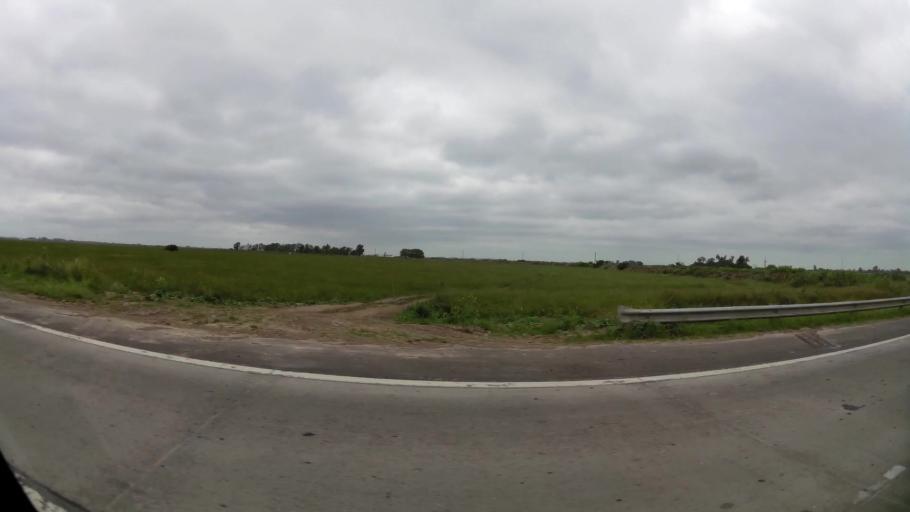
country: AR
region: Buenos Aires
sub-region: Partido de San Vicente
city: San Vicente
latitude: -35.0284
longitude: -58.3583
